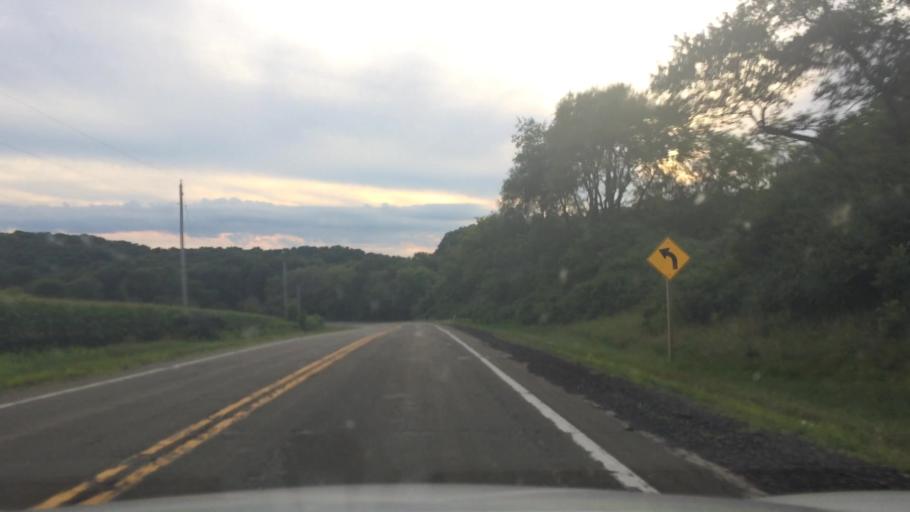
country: US
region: Wisconsin
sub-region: Columbia County
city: Lodi
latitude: 43.3229
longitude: -89.4971
